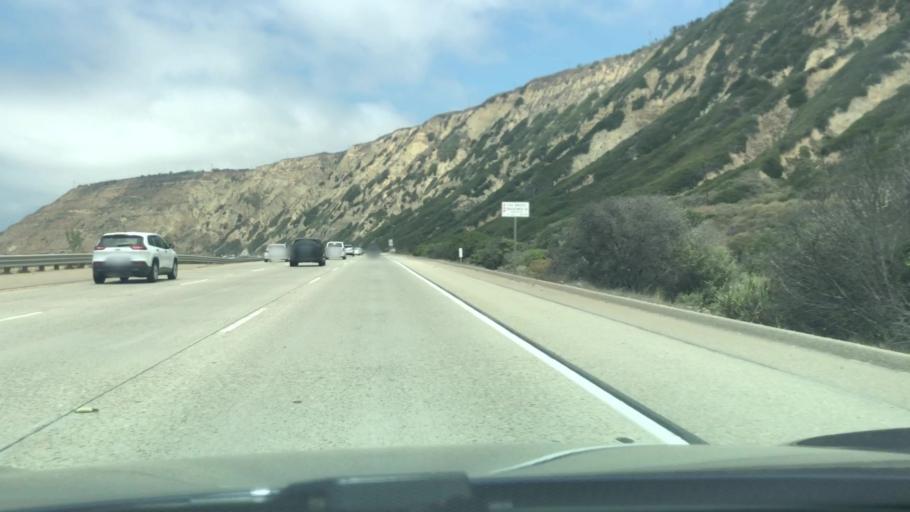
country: US
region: California
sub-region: Santa Barbara County
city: Carpinteria
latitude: 34.3494
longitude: -119.4241
